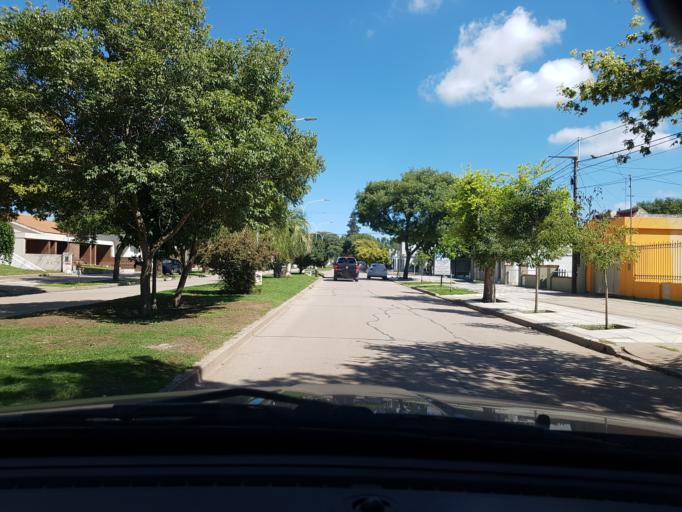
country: AR
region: Cordoba
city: General Cabrera
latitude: -32.7581
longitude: -63.7933
